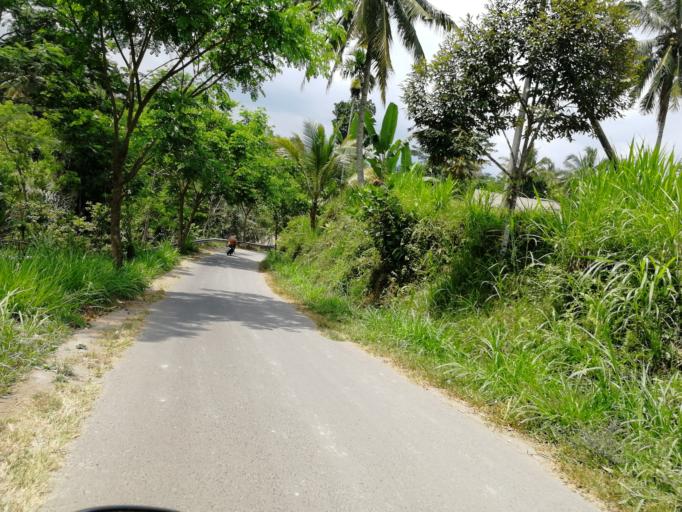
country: ID
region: West Nusa Tenggara
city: Pediti
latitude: -8.5594
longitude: 116.3326
